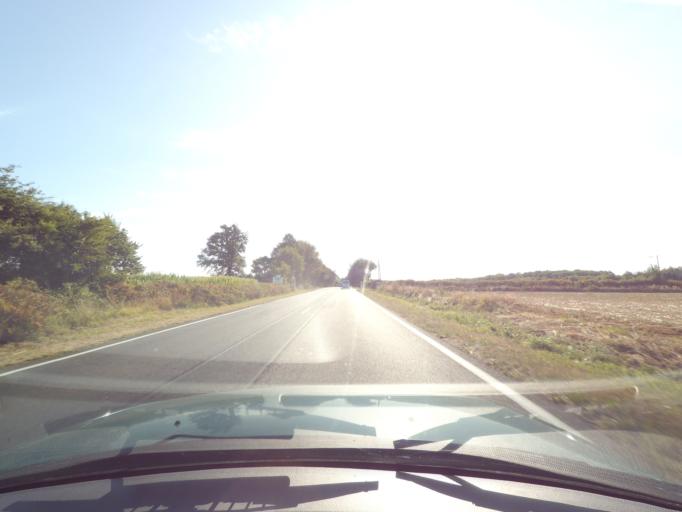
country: FR
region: Poitou-Charentes
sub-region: Departement des Deux-Sevres
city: Thenezay
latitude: 46.6590
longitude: -0.0332
